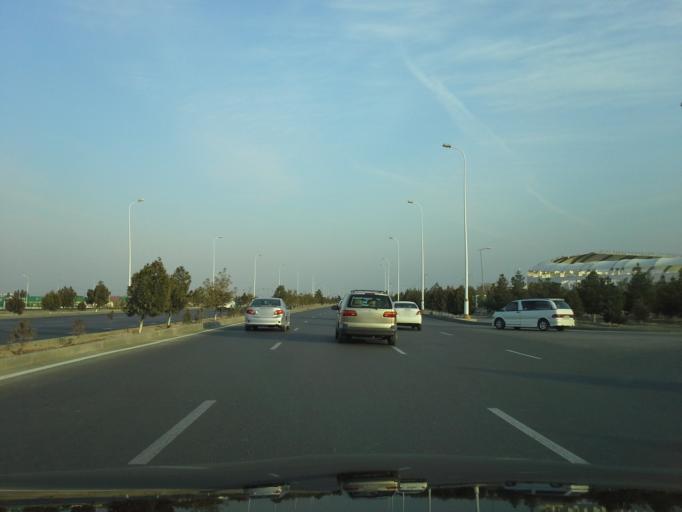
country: TM
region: Ahal
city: Abadan
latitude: 38.0482
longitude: 58.1951
